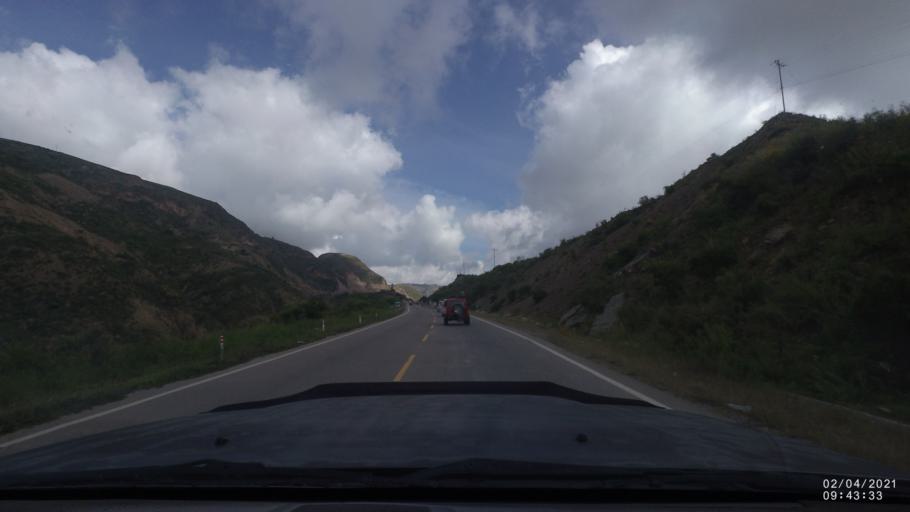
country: BO
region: Cochabamba
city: Irpa Irpa
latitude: -17.6314
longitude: -66.3767
